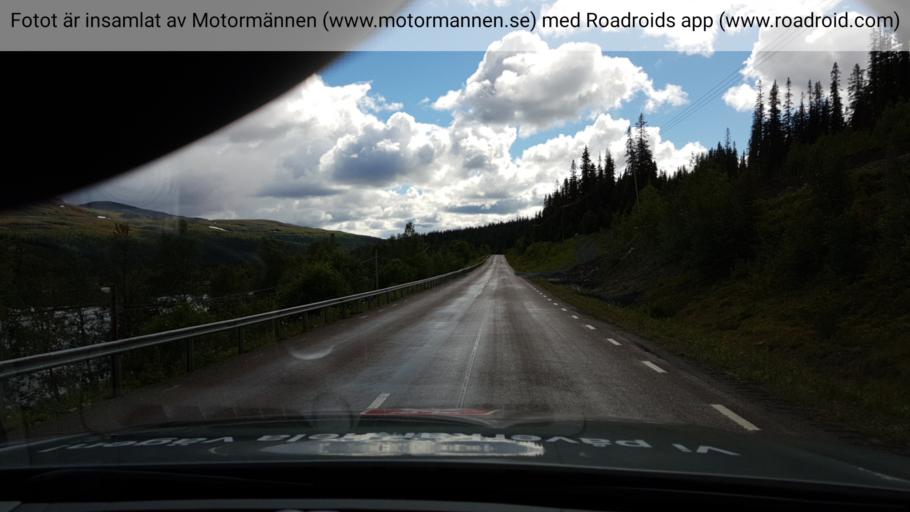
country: SE
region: Jaemtland
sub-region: Are Kommun
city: Jarpen
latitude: 63.0986
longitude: 13.7890
